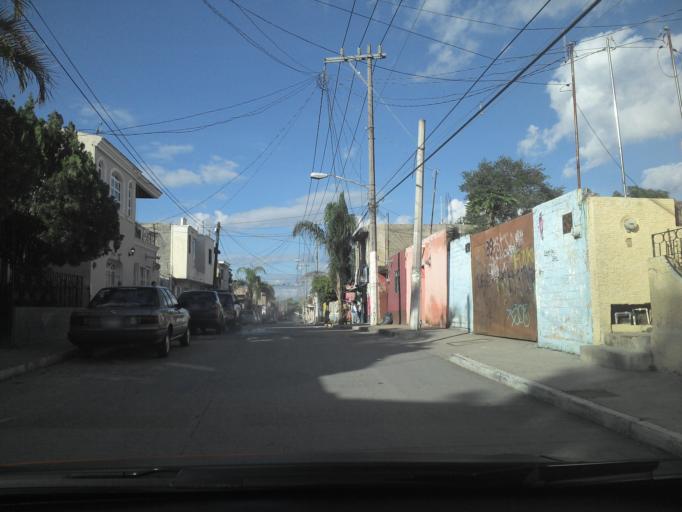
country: MX
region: Jalisco
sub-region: Tlajomulco de Zuniga
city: Palomar
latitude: 20.6198
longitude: -103.4544
